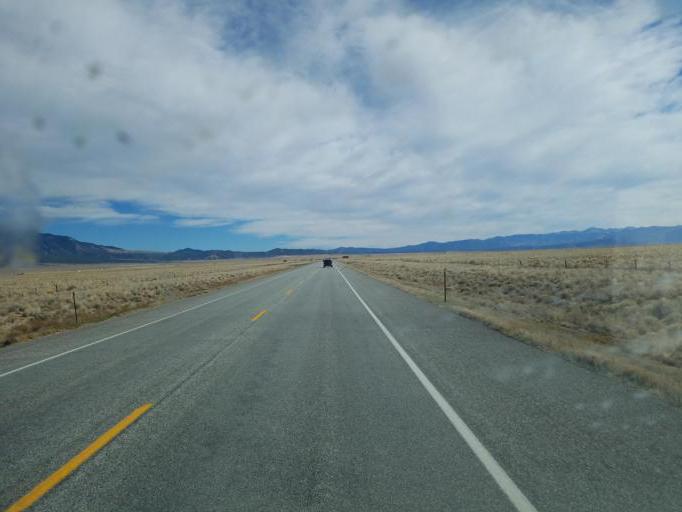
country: US
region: Colorado
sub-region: Alamosa County
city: Alamosa East
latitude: 37.4750
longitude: -105.6242
